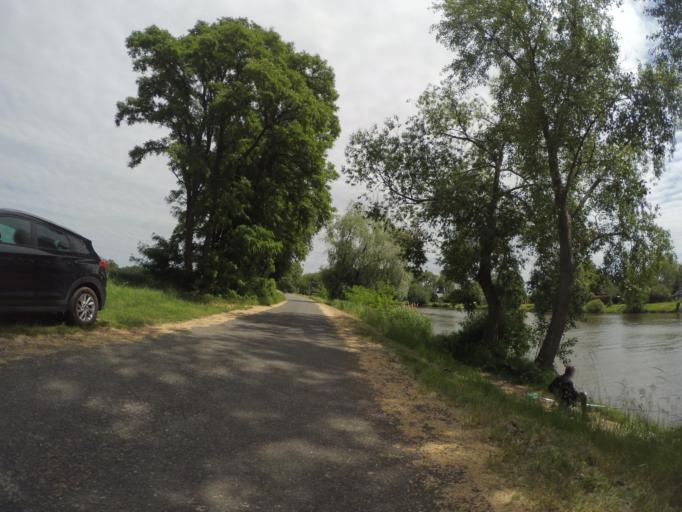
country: CZ
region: Central Bohemia
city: Milovice
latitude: 50.1707
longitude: 14.8812
